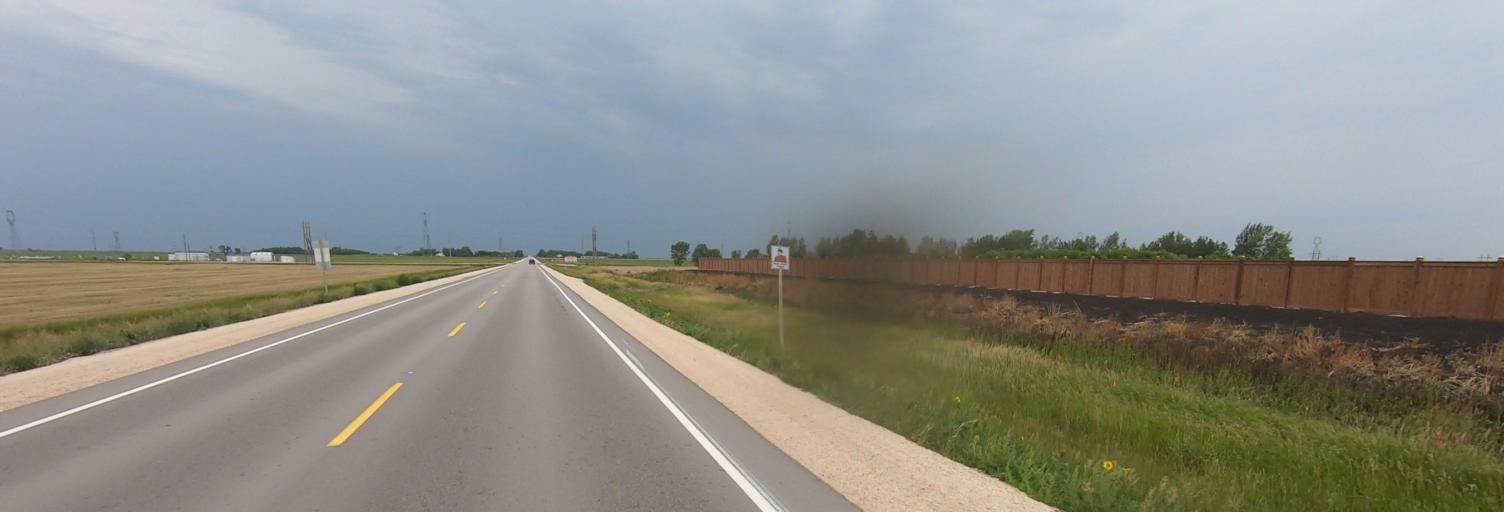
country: CA
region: Manitoba
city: Headingley
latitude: 49.7684
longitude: -97.3401
